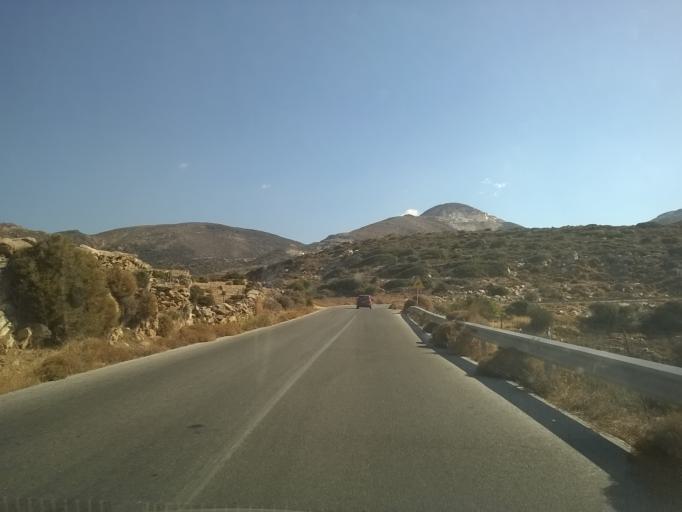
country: GR
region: South Aegean
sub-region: Nomos Kykladon
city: Filotion
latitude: 37.0891
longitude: 25.4497
